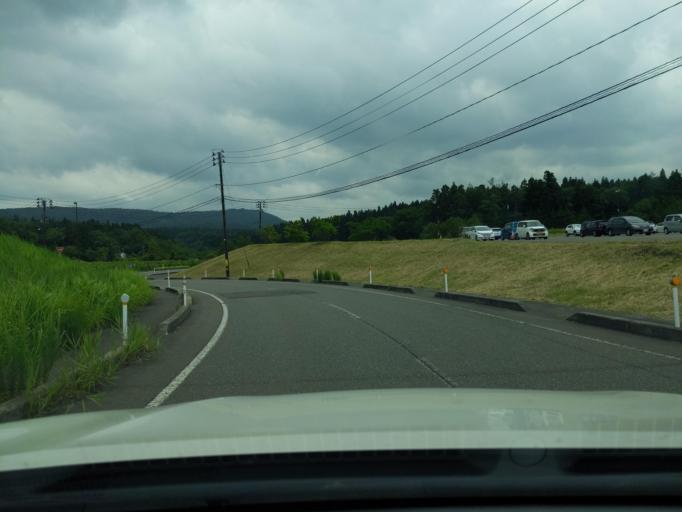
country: JP
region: Niigata
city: Kashiwazaki
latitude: 37.3392
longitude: 138.5880
